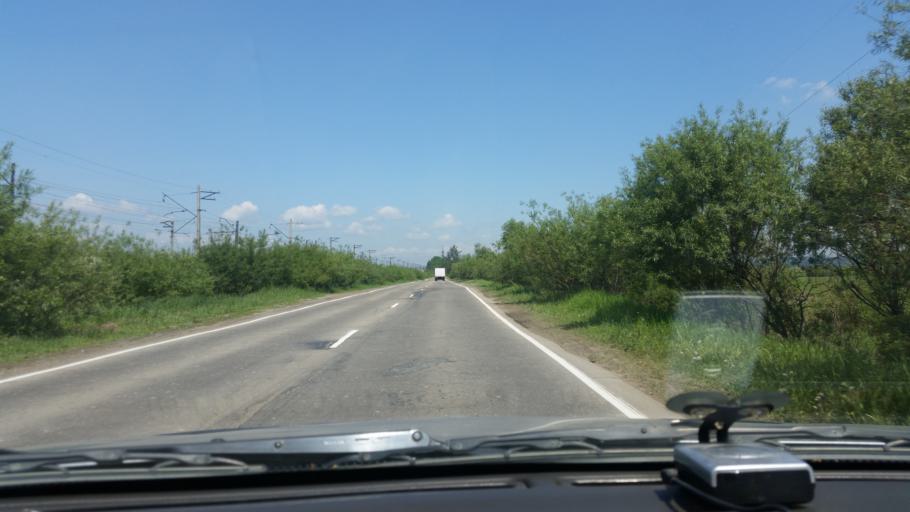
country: RU
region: Irkutsk
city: Shelekhov
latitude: 52.1724
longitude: 104.1076
